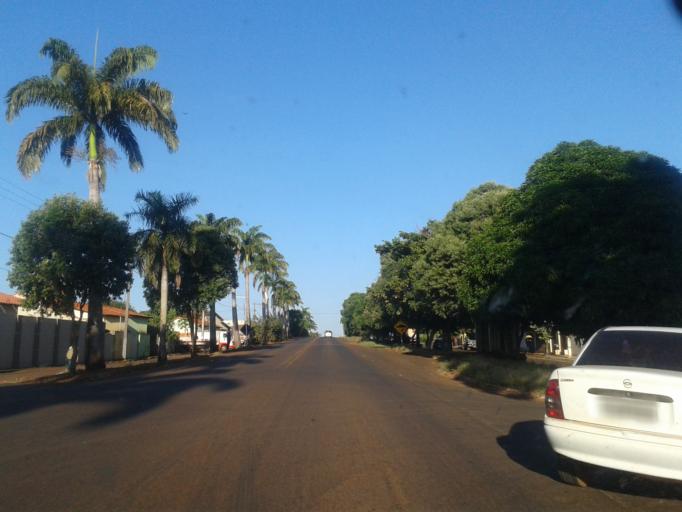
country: BR
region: Minas Gerais
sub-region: Capinopolis
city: Capinopolis
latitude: -18.6884
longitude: -49.5672
